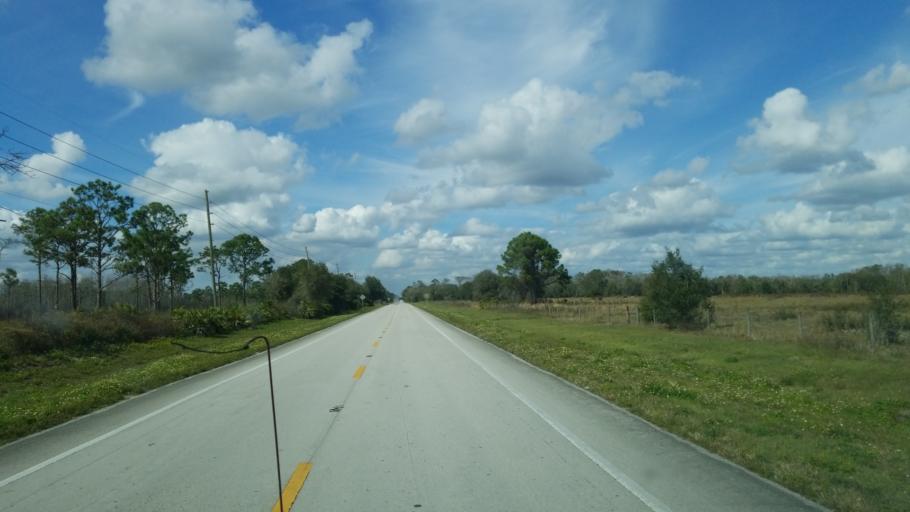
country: US
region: Florida
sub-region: Brevard County
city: June Park
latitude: 27.9586
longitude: -81.0028
